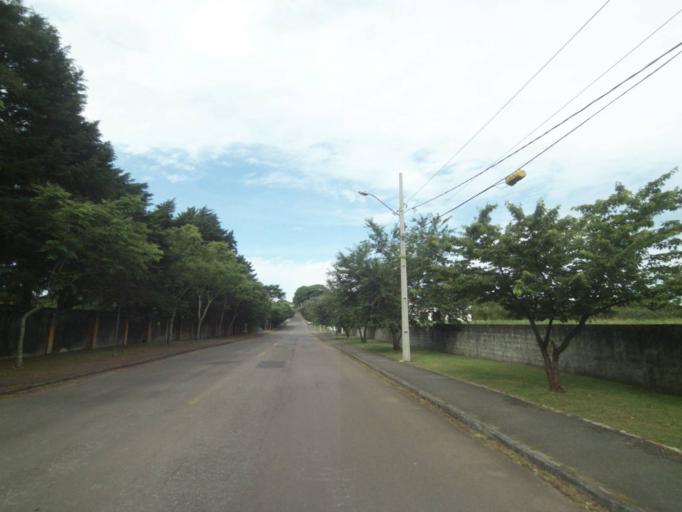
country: BR
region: Parana
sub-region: Pinhais
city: Pinhais
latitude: -25.4206
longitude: -49.2146
